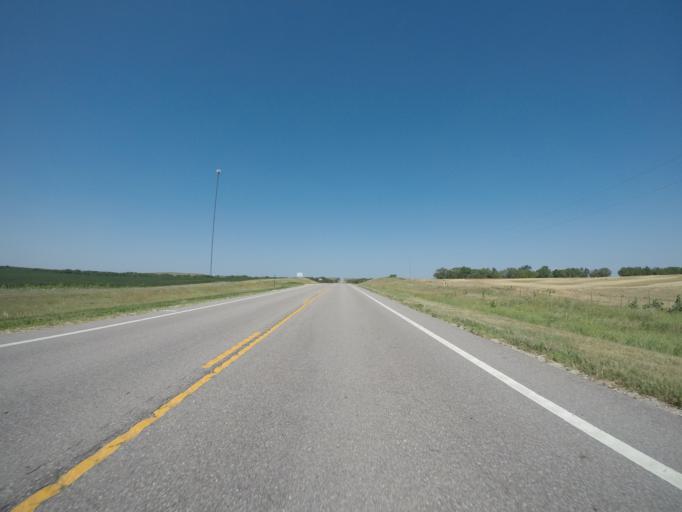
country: US
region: Kansas
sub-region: Cloud County
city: Concordia
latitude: 39.3648
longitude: -97.6552
